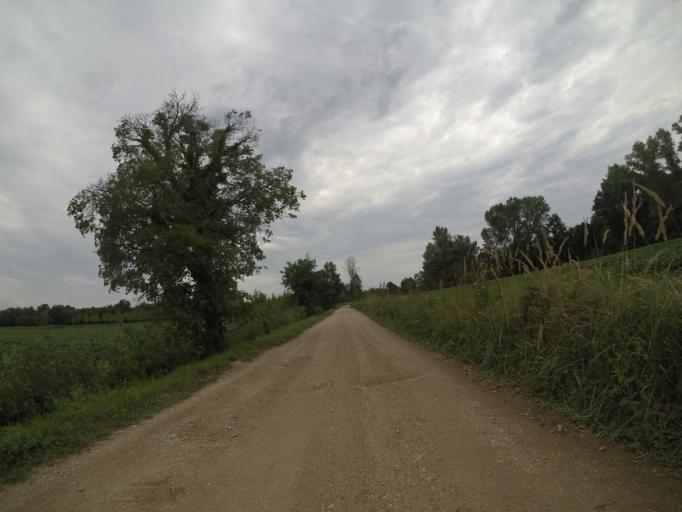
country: IT
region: Friuli Venezia Giulia
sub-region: Provincia di Udine
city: Rivignano
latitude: 45.8965
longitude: 13.0632
